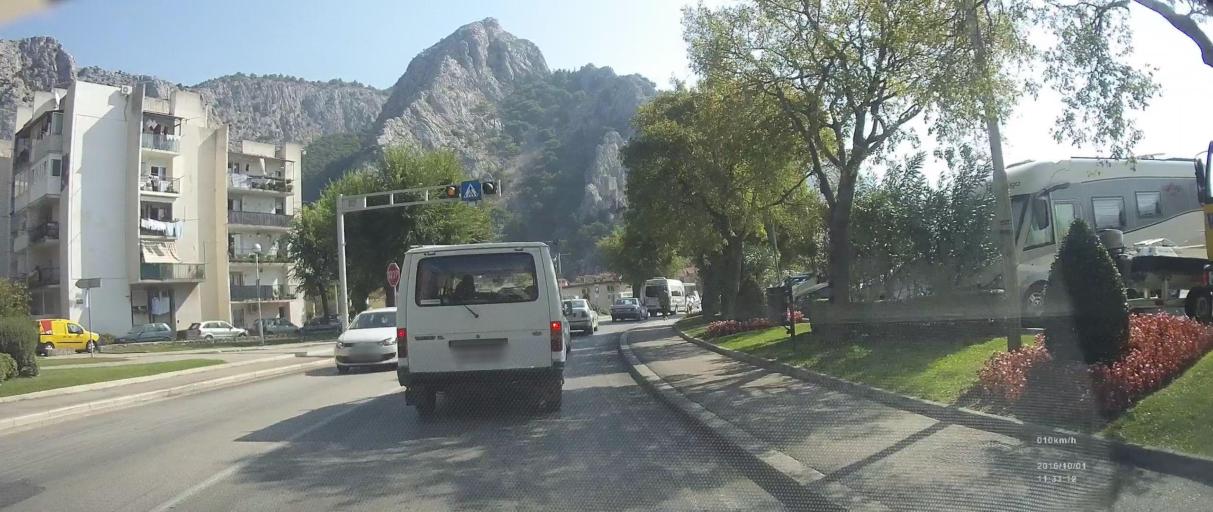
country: HR
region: Splitsko-Dalmatinska
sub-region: Grad Omis
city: Omis
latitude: 43.4459
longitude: 16.6893
